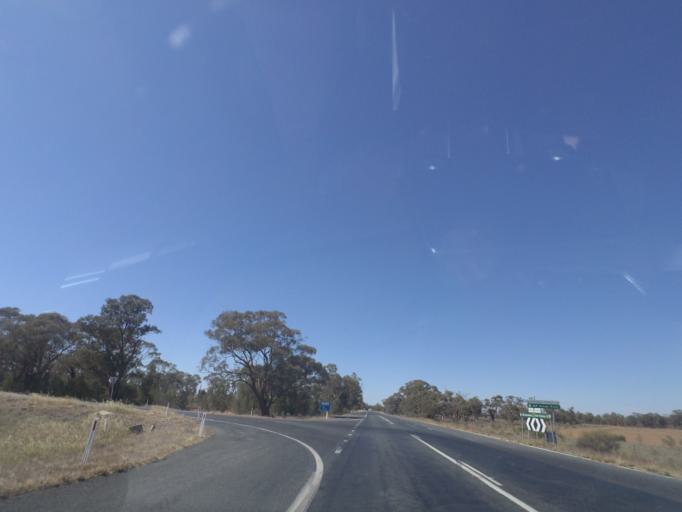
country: AU
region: New South Wales
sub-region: Bland
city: West Wyalong
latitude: -34.1934
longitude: 147.1113
